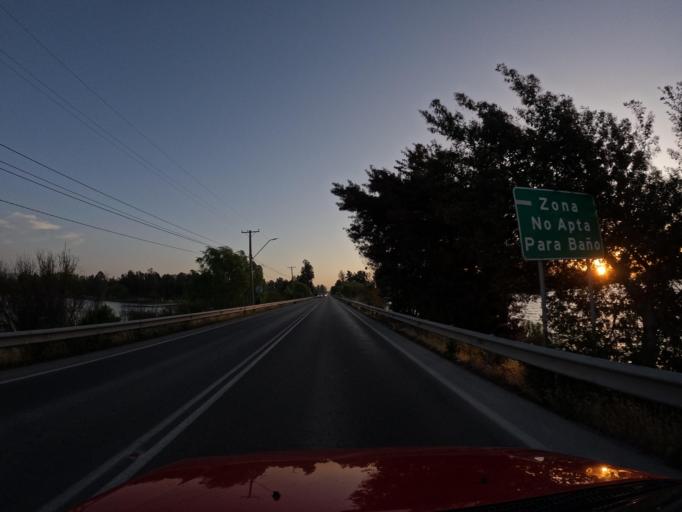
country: CL
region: O'Higgins
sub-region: Provincia de Cachapoal
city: San Vicente
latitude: -34.1494
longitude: -71.3832
